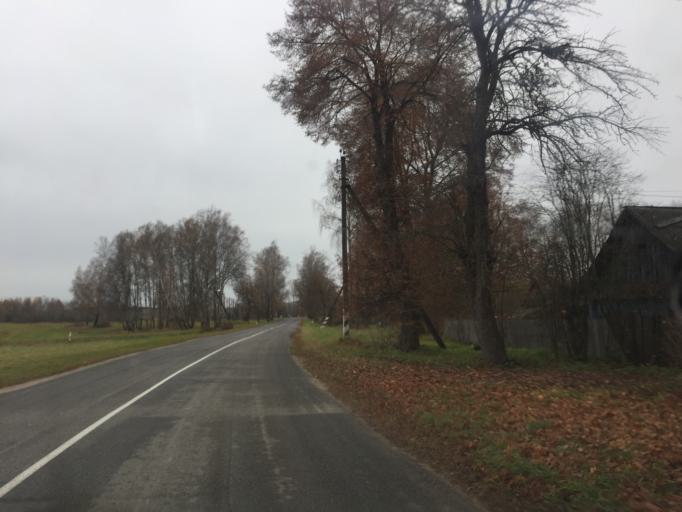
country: BY
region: Mogilev
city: Chavusy
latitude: 53.8817
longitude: 31.0532
